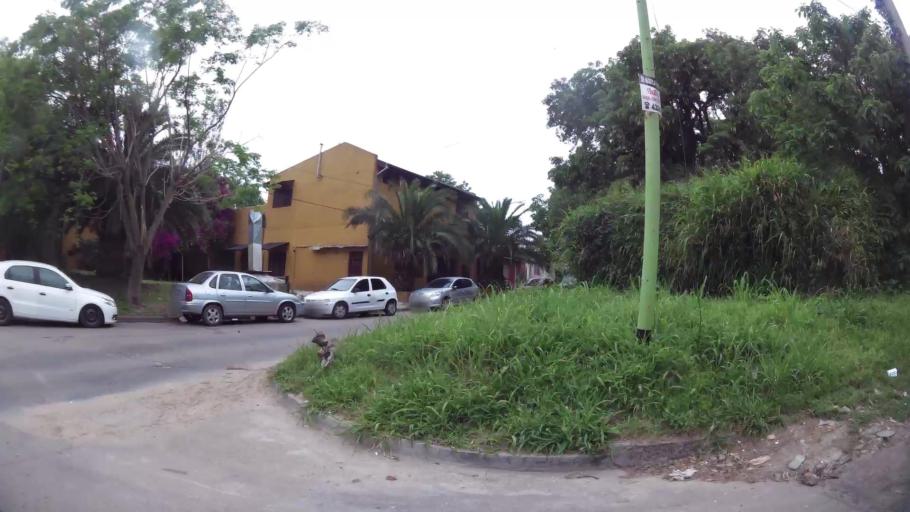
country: AR
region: Buenos Aires
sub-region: Partido de Campana
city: Campana
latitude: -34.1579
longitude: -58.9554
